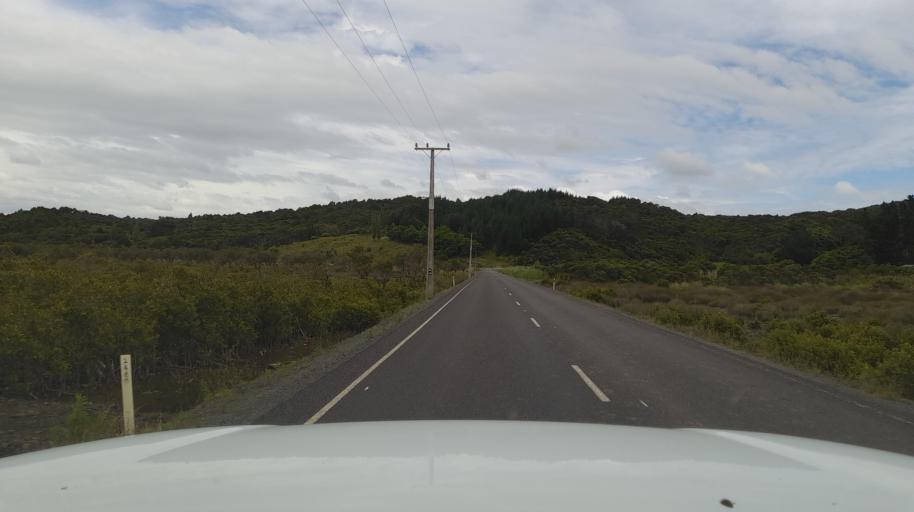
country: NZ
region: Northland
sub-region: Far North District
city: Kaitaia
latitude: -35.4048
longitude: 173.3823
